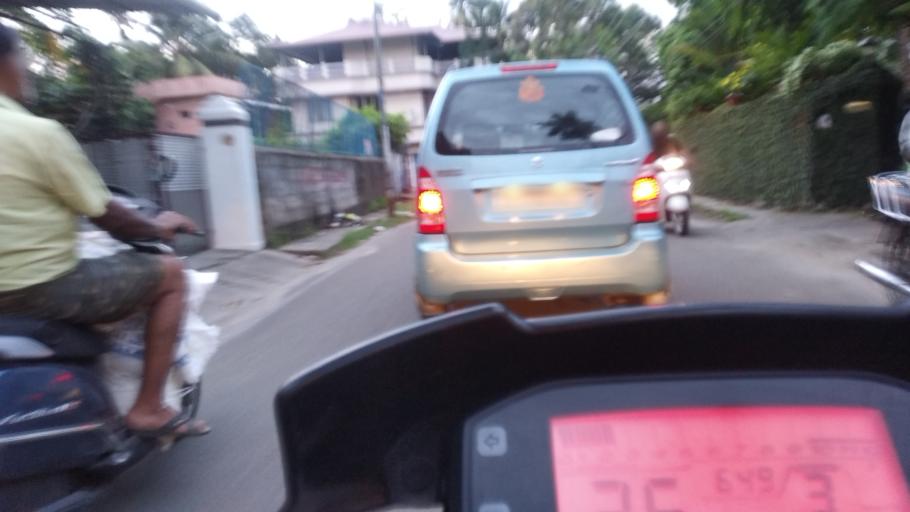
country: IN
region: Kerala
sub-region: Ernakulam
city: Elur
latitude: 10.0106
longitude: 76.2758
